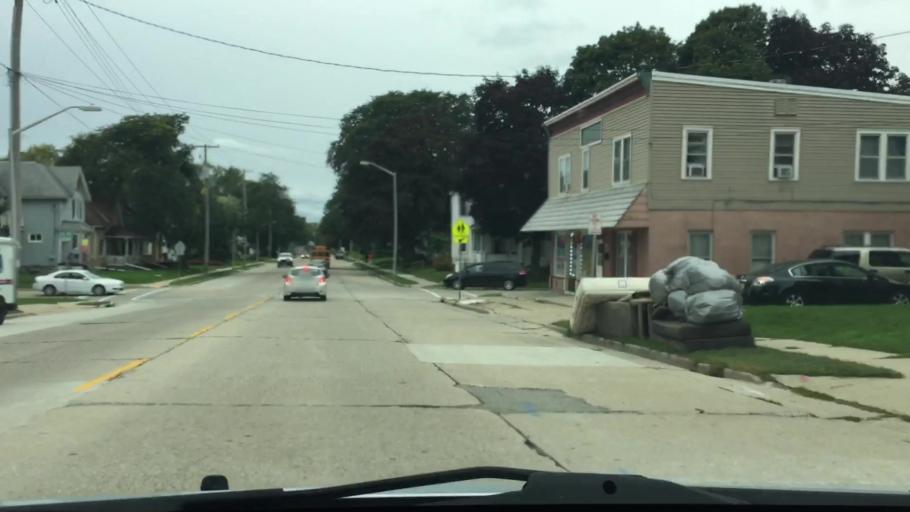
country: US
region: Wisconsin
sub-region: Waukesha County
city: Waukesha
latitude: 43.0130
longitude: -88.2161
